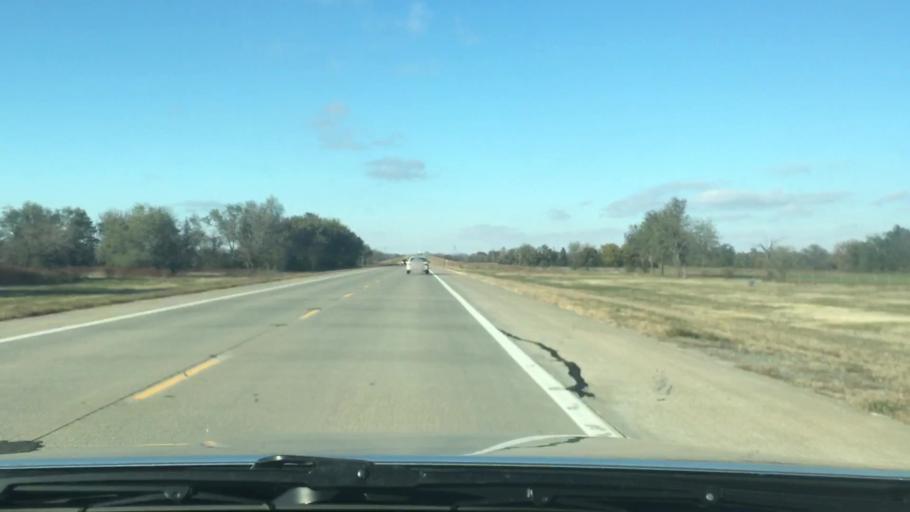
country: US
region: Kansas
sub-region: Reno County
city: Hutchinson
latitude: 38.0718
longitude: -97.9873
